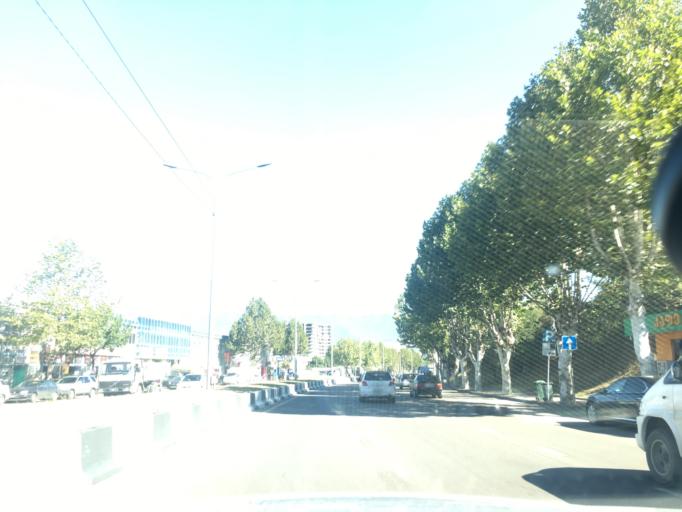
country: GE
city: Zahesi
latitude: 41.7791
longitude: 44.7962
